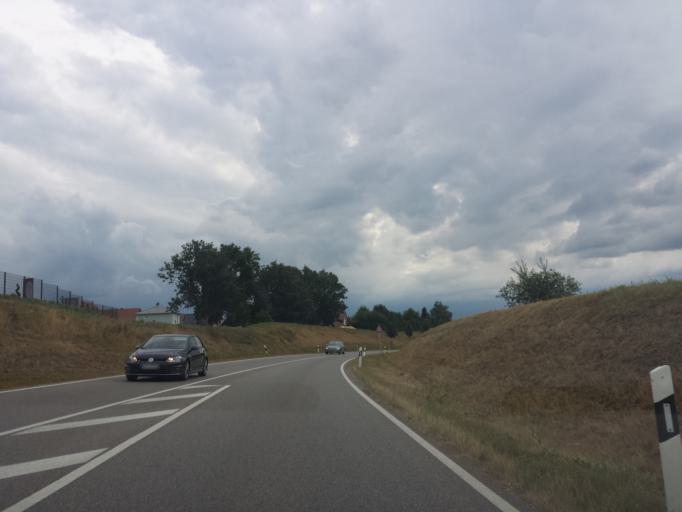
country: DE
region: Bavaria
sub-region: Swabia
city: Burgau
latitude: 48.4401
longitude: 10.3836
